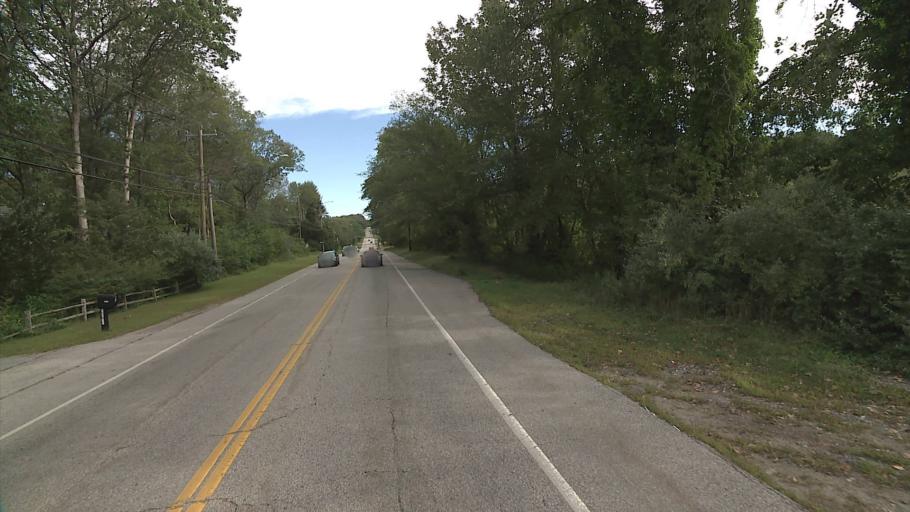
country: US
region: Connecticut
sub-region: New London County
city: Uncasville
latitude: 41.4576
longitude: -72.1053
